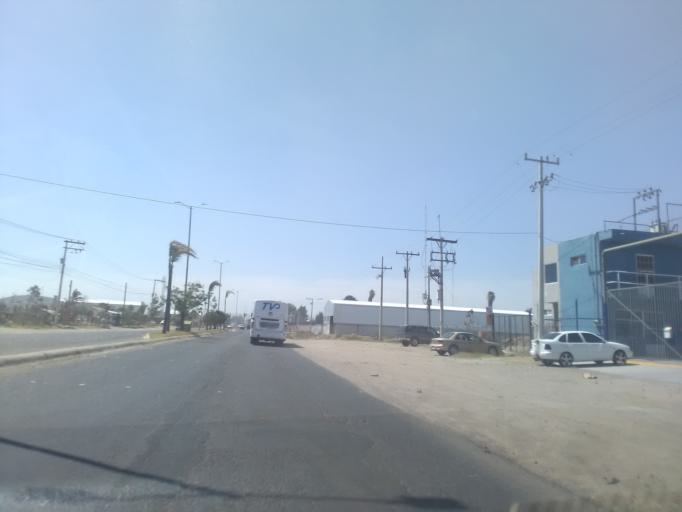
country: MX
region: Durango
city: Victoria de Durango
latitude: 24.0299
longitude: -104.6077
